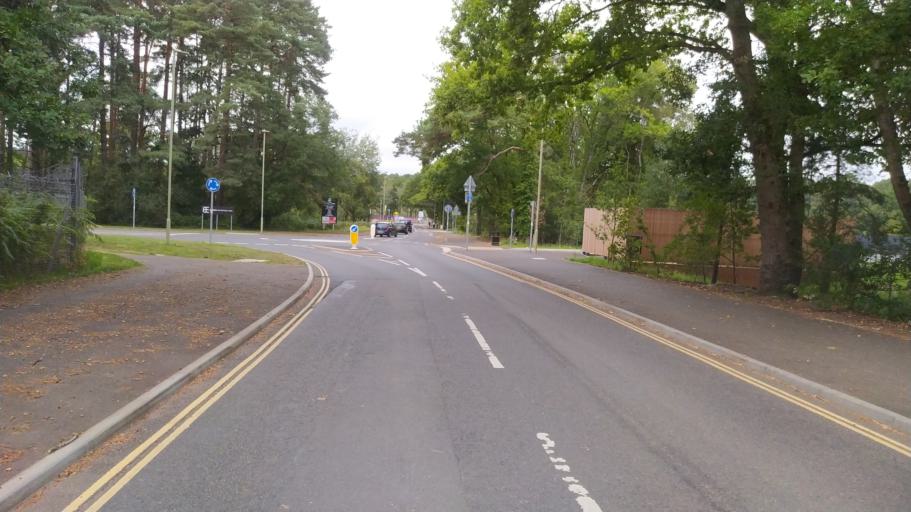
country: GB
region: England
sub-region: Hampshire
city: Bordon
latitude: 51.1172
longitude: -0.8690
